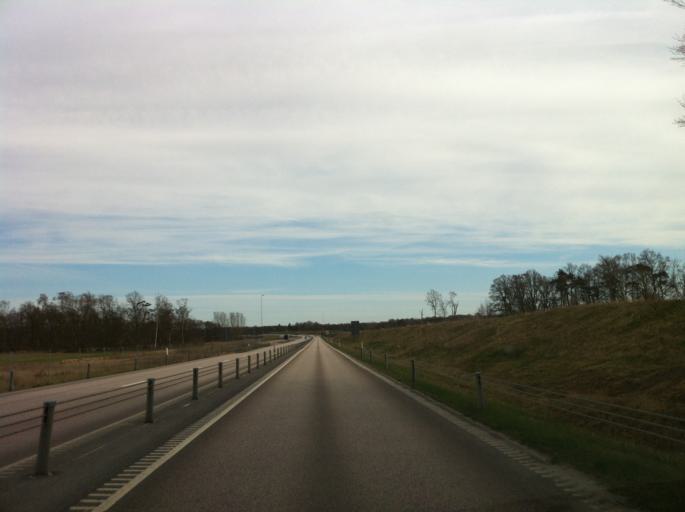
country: SE
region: Skane
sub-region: Helsingborg
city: Helsingborg
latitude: 56.1033
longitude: 12.6626
